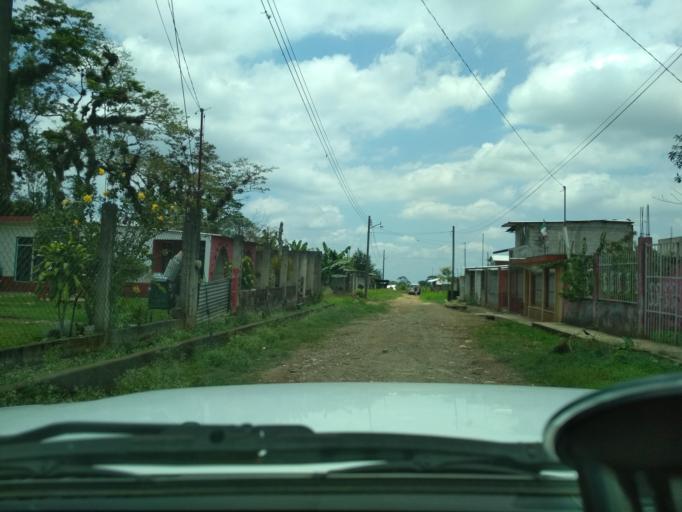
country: MX
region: Veracruz
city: Tocuila
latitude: 18.9505
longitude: -97.0165
